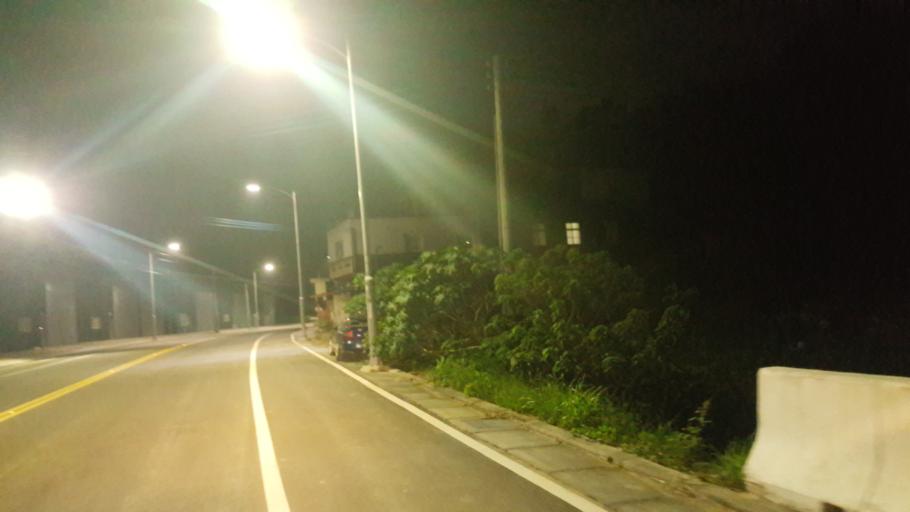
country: TW
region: Taiwan
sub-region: Hsinchu
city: Hsinchu
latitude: 24.7555
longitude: 120.9732
